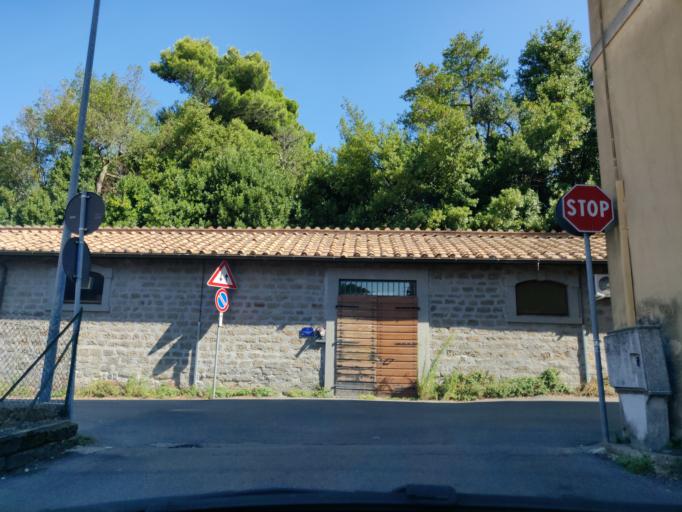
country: IT
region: Latium
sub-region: Provincia di Viterbo
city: Viterbo
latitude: 42.4307
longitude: 12.1284
